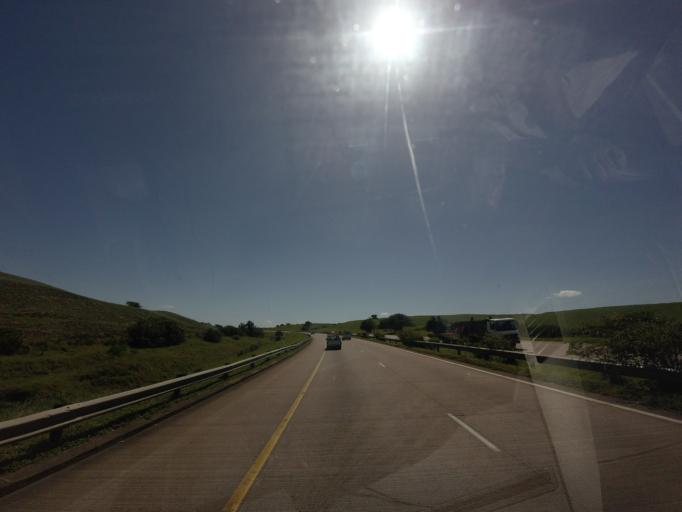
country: ZA
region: KwaZulu-Natal
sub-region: iLembe District Municipality
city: Stanger
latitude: -29.4374
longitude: 31.2651
